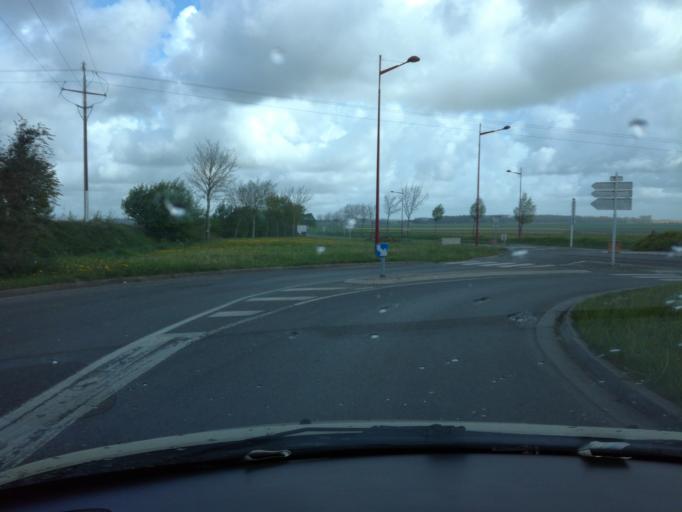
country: FR
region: Picardie
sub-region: Departement de la Somme
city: Oisemont
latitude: 49.9620
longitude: 1.7615
